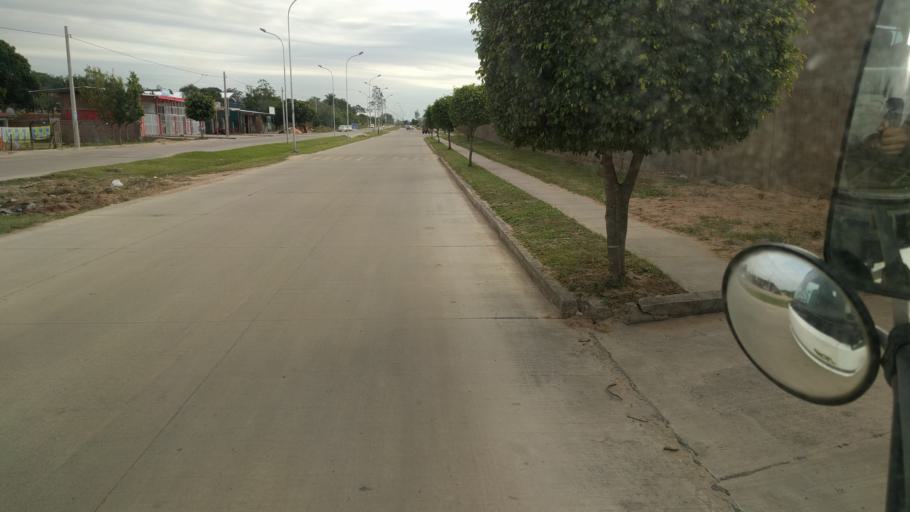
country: BO
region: Santa Cruz
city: Santa Cruz de la Sierra
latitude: -17.6831
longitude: -63.1520
